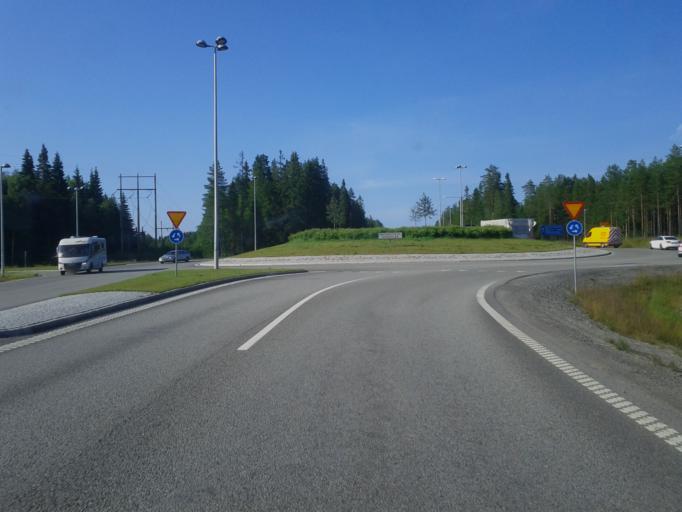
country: SE
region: Vaesterbotten
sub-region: Umea Kommun
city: Ersmark
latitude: 63.8179
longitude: 20.3277
